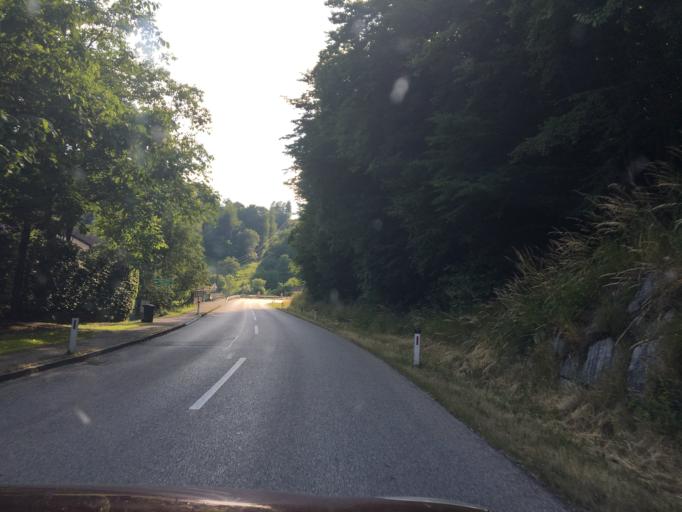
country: AT
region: Upper Austria
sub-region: Politischer Bezirk Urfahr-Umgebung
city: Gallneukirchen
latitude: 48.3666
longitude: 14.4044
